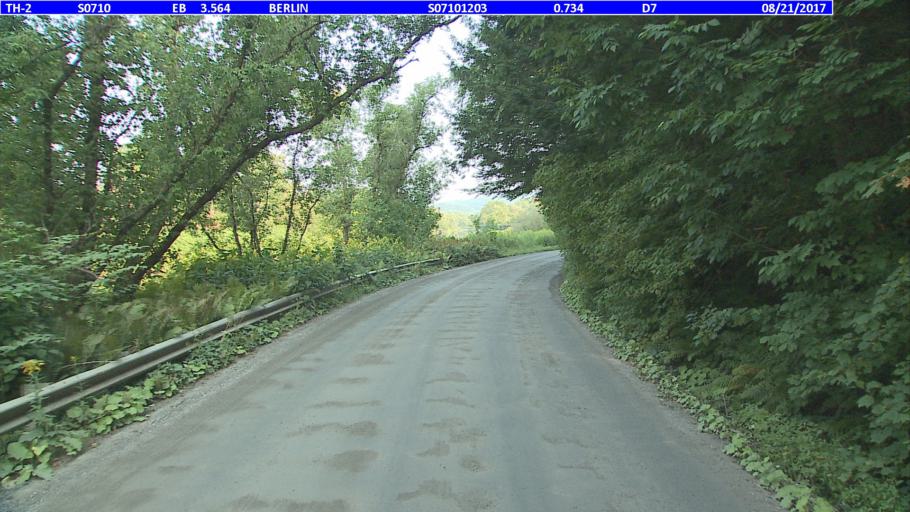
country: US
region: Vermont
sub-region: Washington County
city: Montpelier
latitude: 44.2644
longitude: -72.6277
